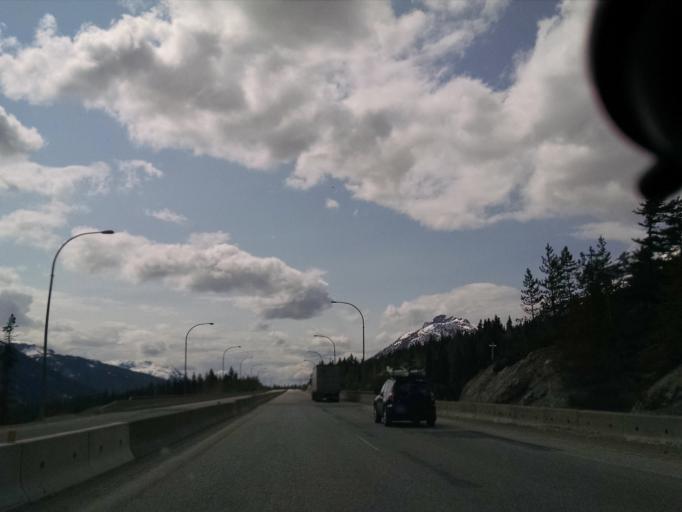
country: CA
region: British Columbia
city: Hope
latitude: 49.6188
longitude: -121.0430
